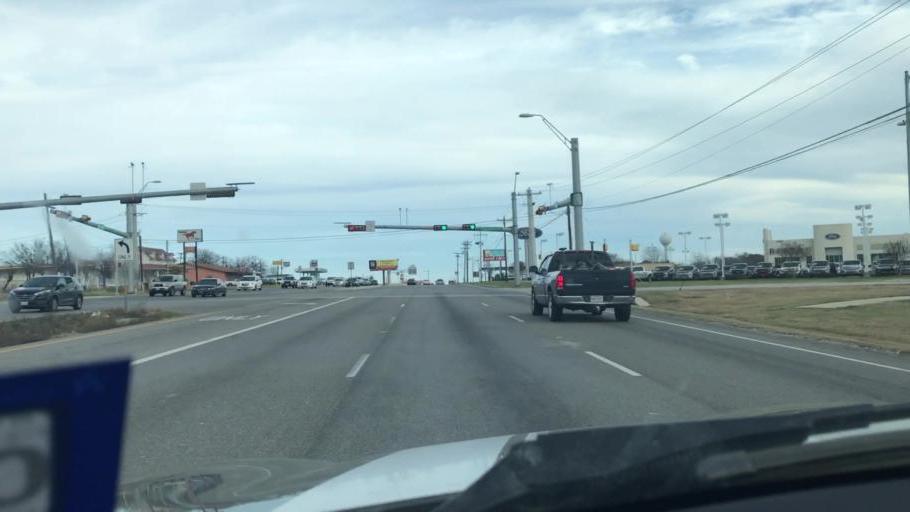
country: US
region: Texas
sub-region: Travis County
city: Manor
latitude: 30.3479
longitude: -97.5630
